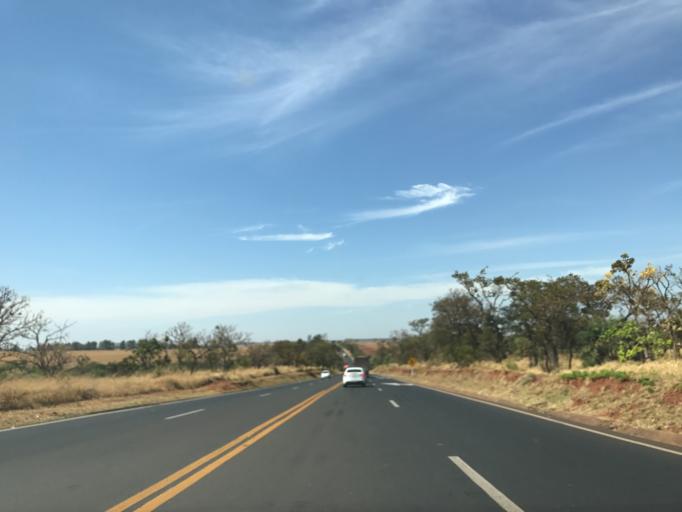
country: BR
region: Minas Gerais
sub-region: Monte Alegre De Minas
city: Monte Alegre de Minas
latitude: -18.8986
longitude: -49.0432
